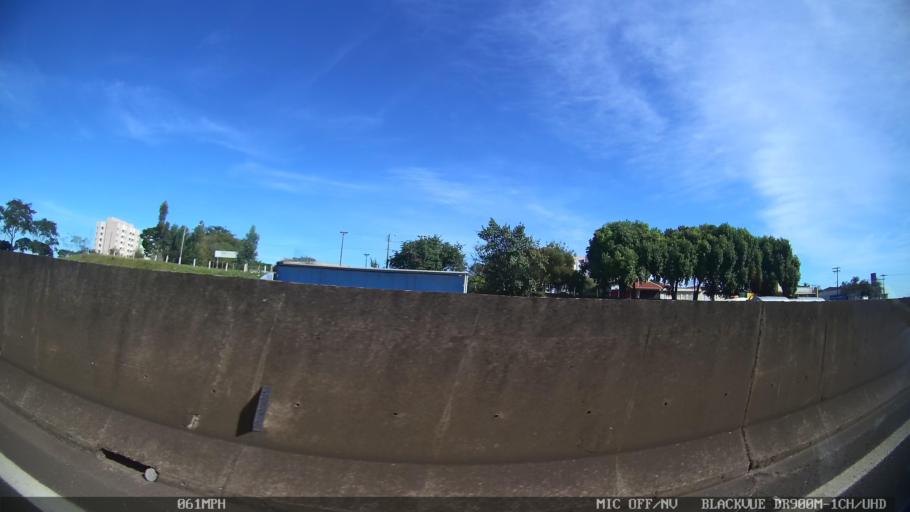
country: BR
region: Sao Paulo
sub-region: Araras
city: Araras
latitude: -22.3555
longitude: -47.3947
